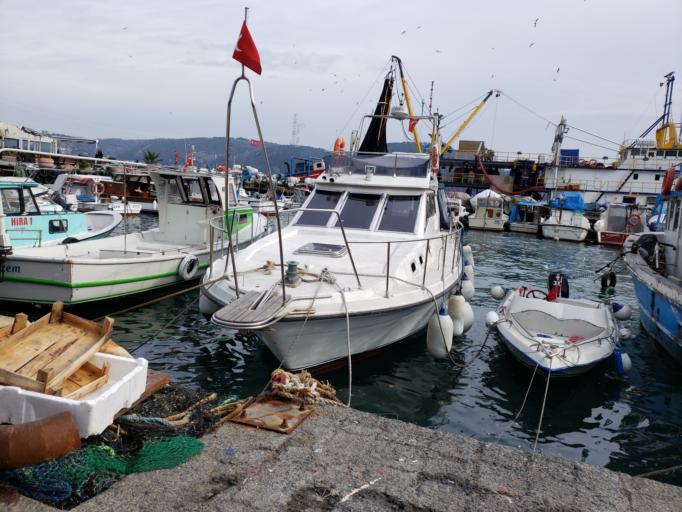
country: TR
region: Istanbul
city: Arikoey
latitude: 41.1687
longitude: 29.0580
